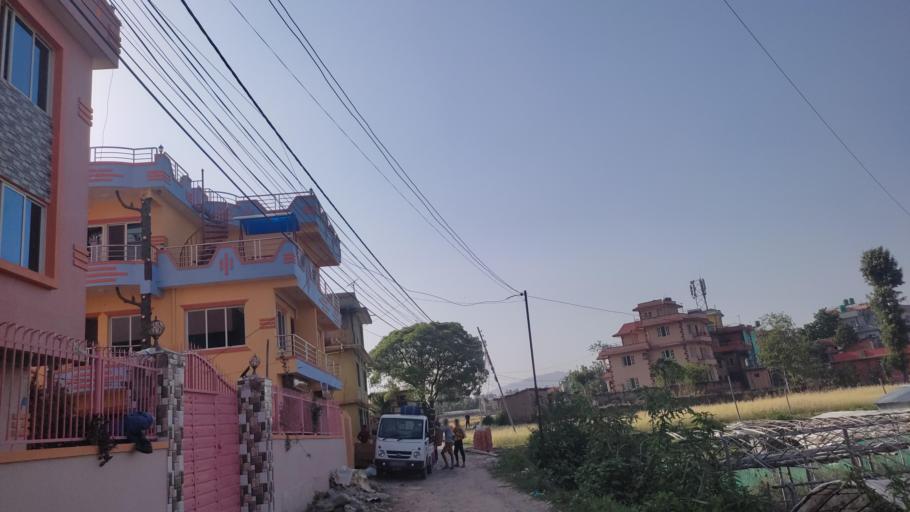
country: NP
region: Central Region
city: Kirtipur
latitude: 27.6606
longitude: 85.2787
